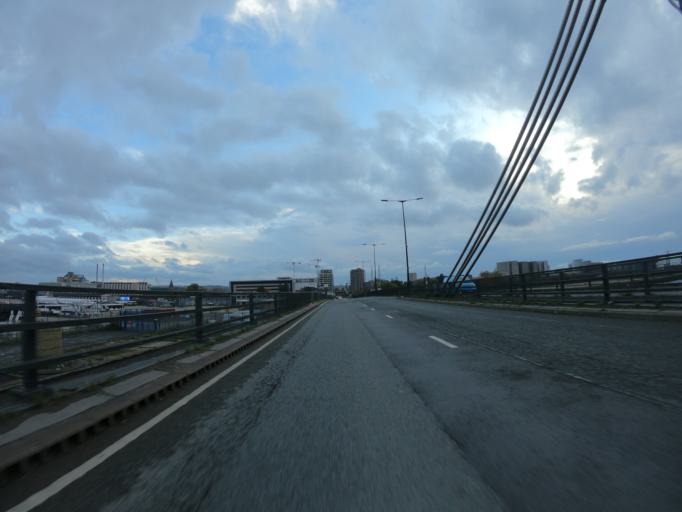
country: GB
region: England
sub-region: Greater London
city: East Ham
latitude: 51.5065
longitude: 0.0400
